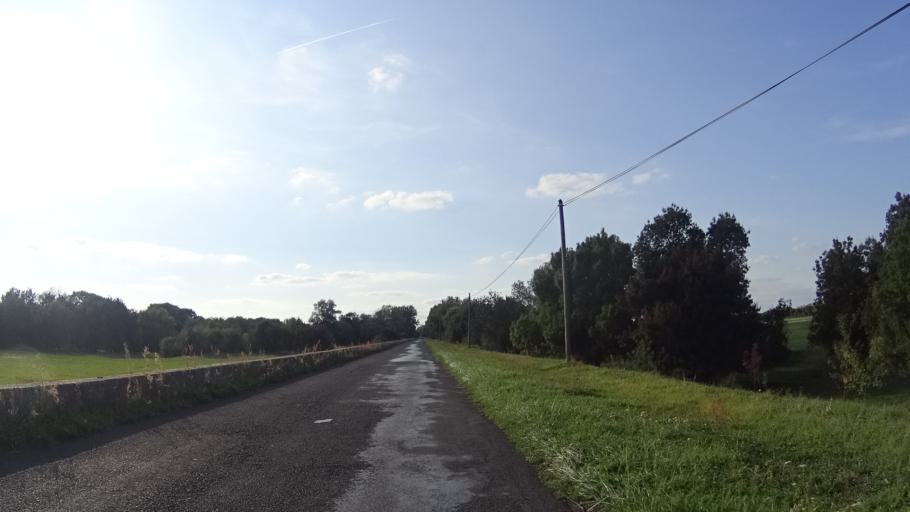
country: FR
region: Pays de la Loire
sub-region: Departement de Maine-et-Loire
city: Chalonnes-sur-Loire
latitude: 47.3721
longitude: -0.7612
